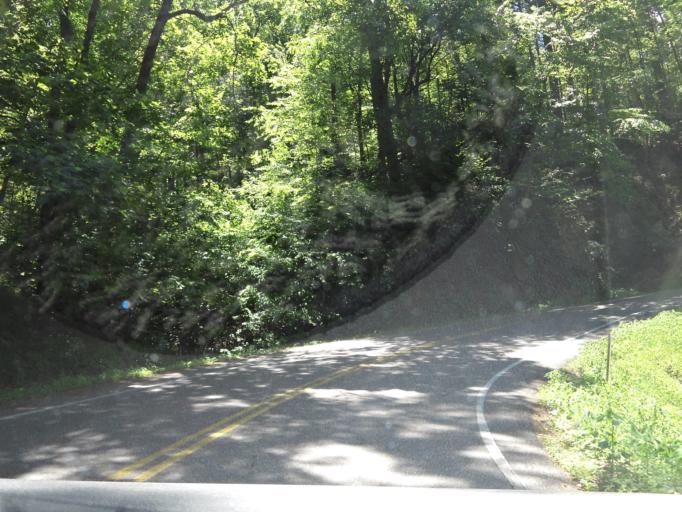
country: US
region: North Carolina
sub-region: Graham County
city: Robbinsville
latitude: 35.4943
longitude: -83.9278
